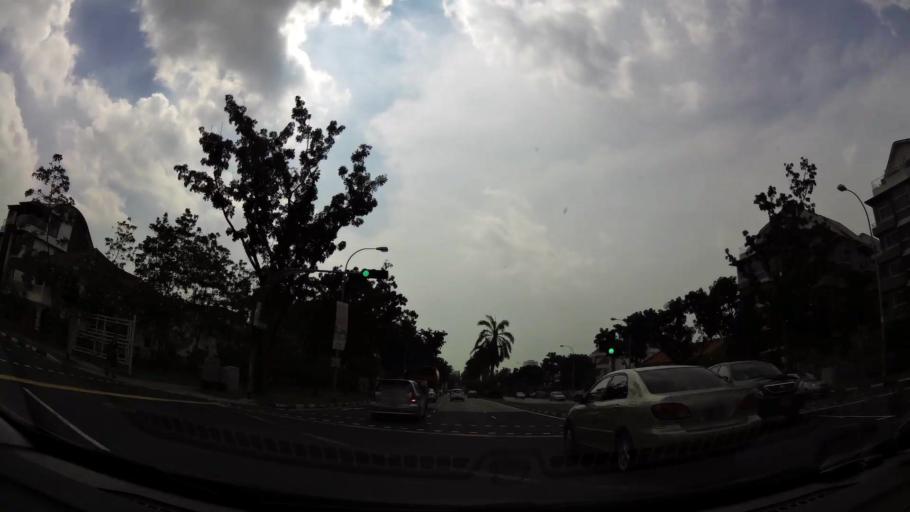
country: SG
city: Singapore
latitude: 1.3132
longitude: 103.9068
